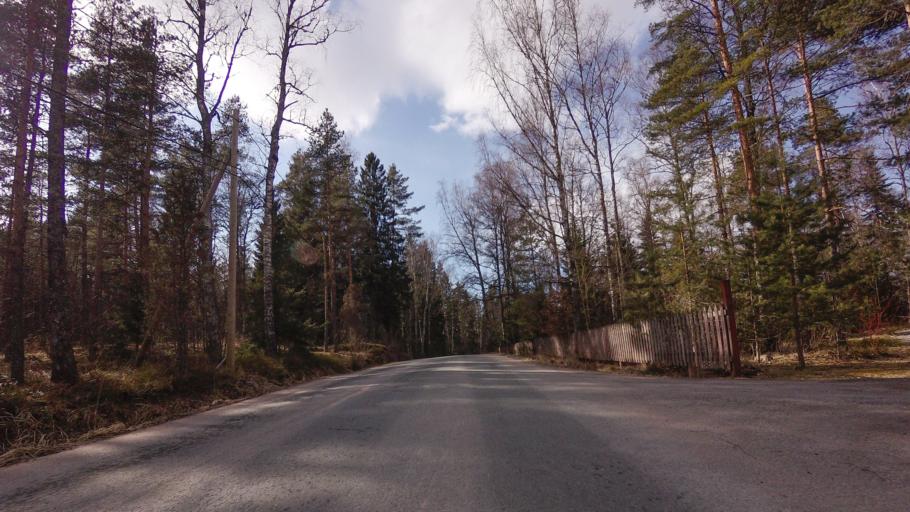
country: FI
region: Varsinais-Suomi
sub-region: Salo
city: Suomusjaervi
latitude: 60.3403
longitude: 23.6963
